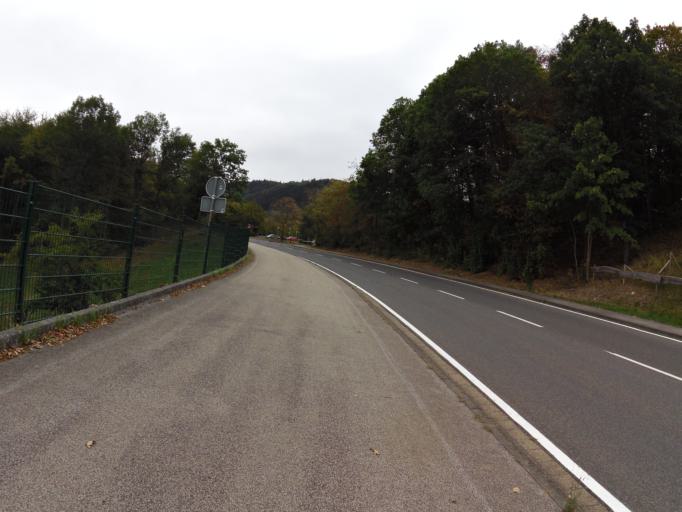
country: DE
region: North Rhine-Westphalia
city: Heimbach
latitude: 50.6348
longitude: 6.4427
